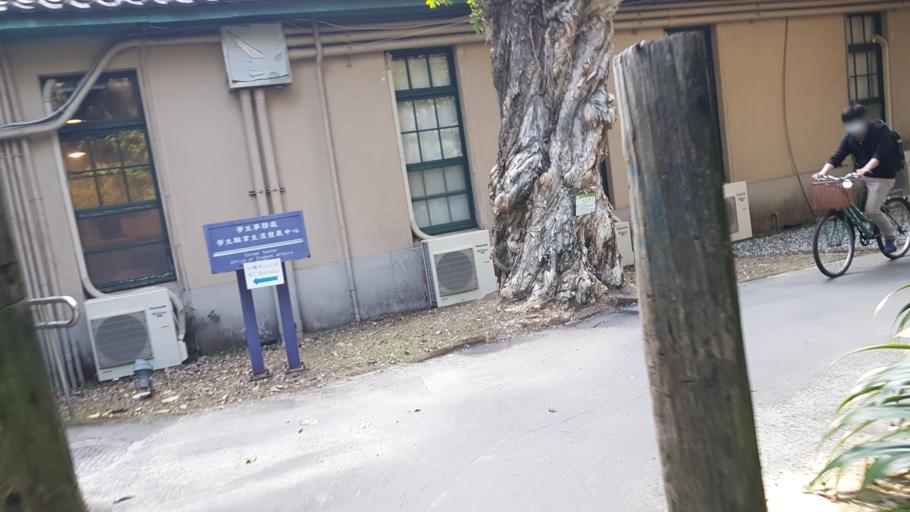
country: TW
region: Taipei
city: Taipei
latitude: 25.0152
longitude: 121.5366
